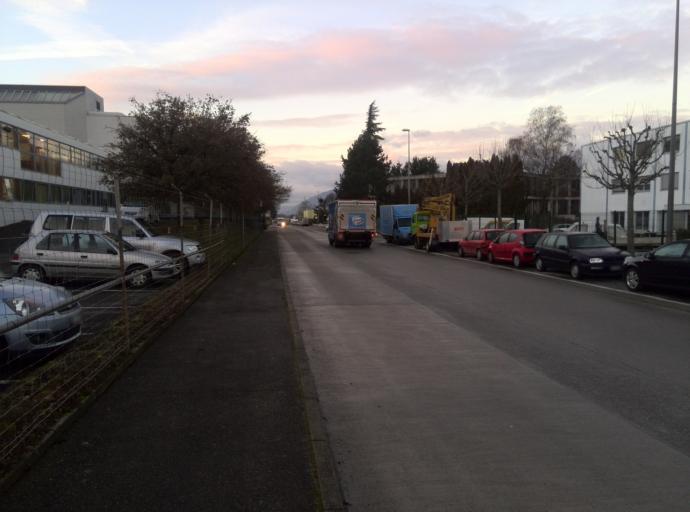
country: CH
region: Geneva
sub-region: Geneva
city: Meyrin
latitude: 46.2278
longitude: 6.0630
